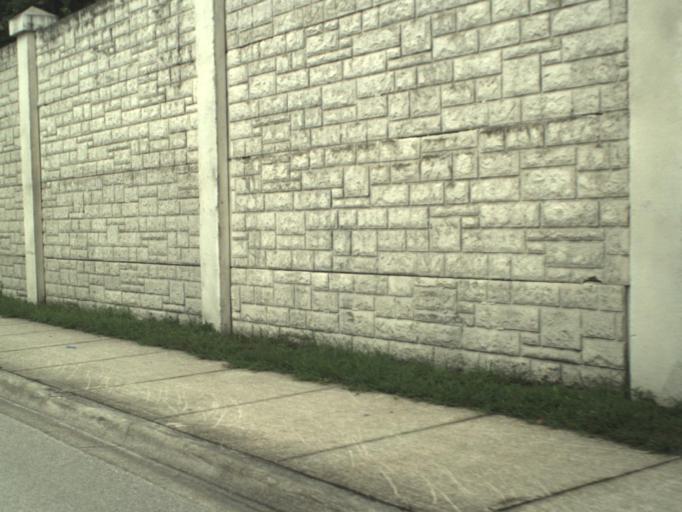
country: US
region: Florida
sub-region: Palm Beach County
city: Mangonia Park
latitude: 26.7533
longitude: -80.1089
